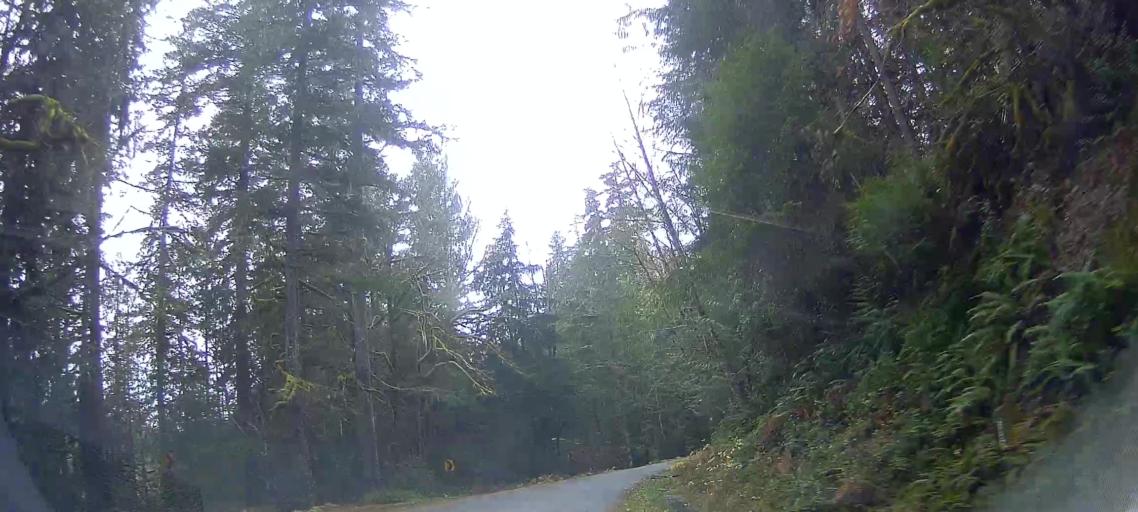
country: US
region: Washington
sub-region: Snohomish County
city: Darrington
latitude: 48.5235
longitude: -121.3836
